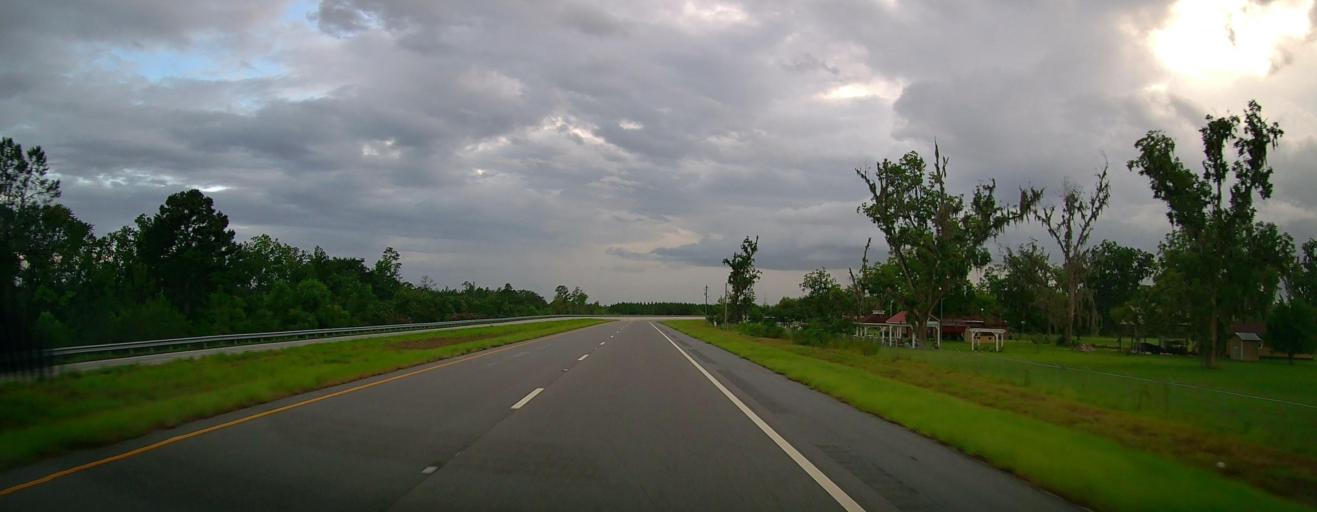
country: US
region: Georgia
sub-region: Ware County
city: Deenwood
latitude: 31.1520
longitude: -82.4430
